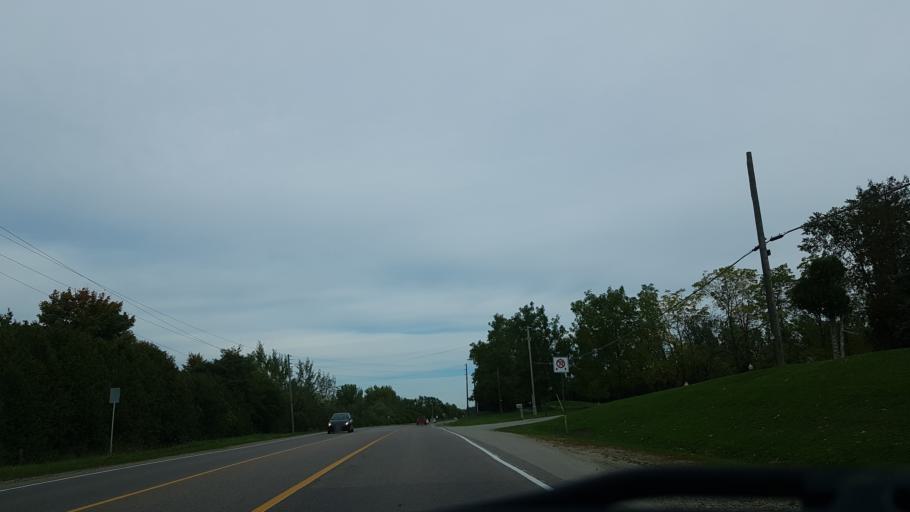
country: CA
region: Ontario
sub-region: Wellington County
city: Guelph
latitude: 43.6013
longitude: -80.2317
